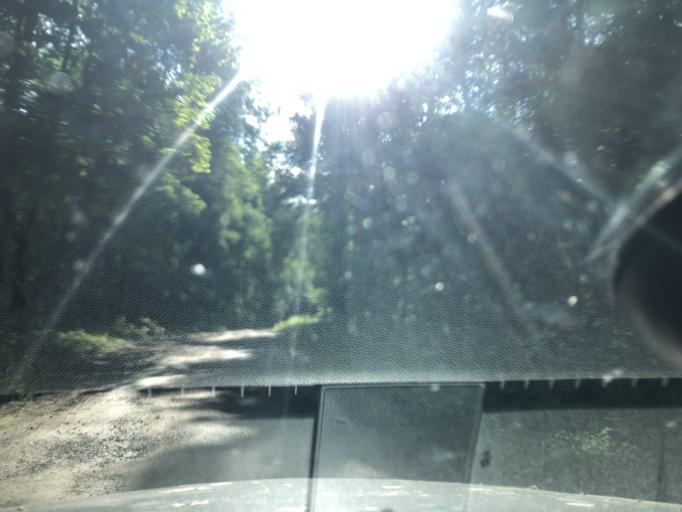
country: RU
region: Tula
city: Shvartsevskiy
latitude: 54.2563
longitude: 37.9215
